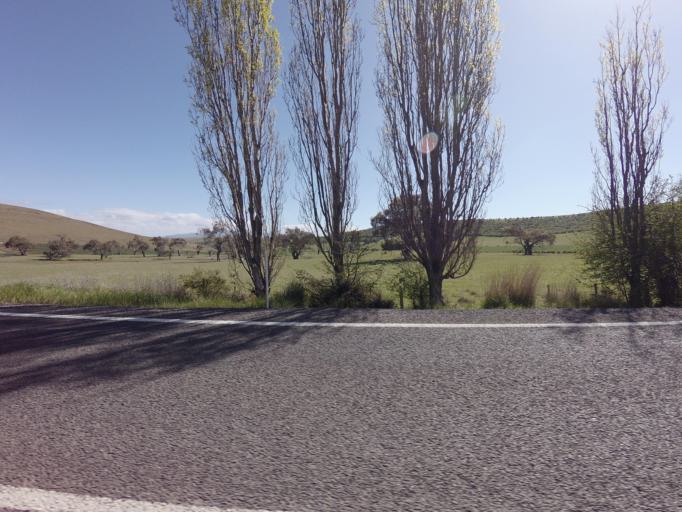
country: AU
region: Tasmania
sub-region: Derwent Valley
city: New Norfolk
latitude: -42.5696
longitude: 146.8808
